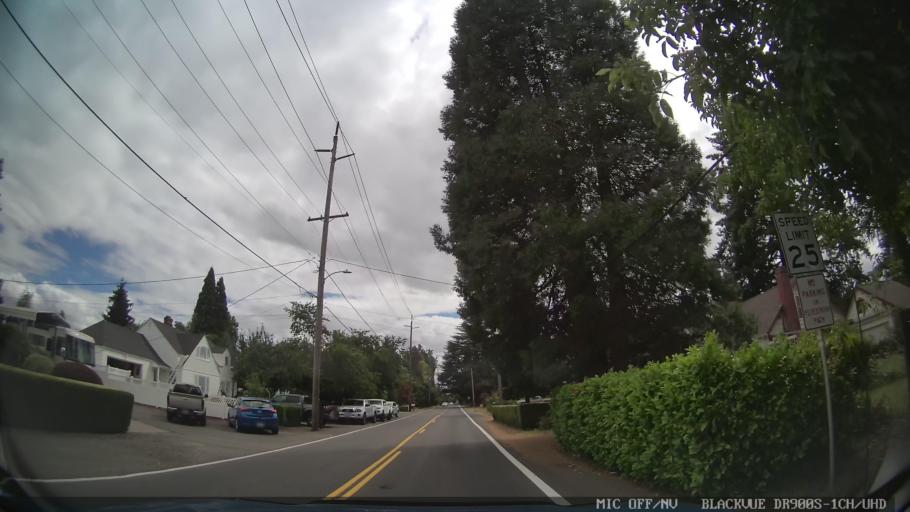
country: US
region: Oregon
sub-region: Marion County
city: Four Corners
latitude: 44.9536
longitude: -123.0009
